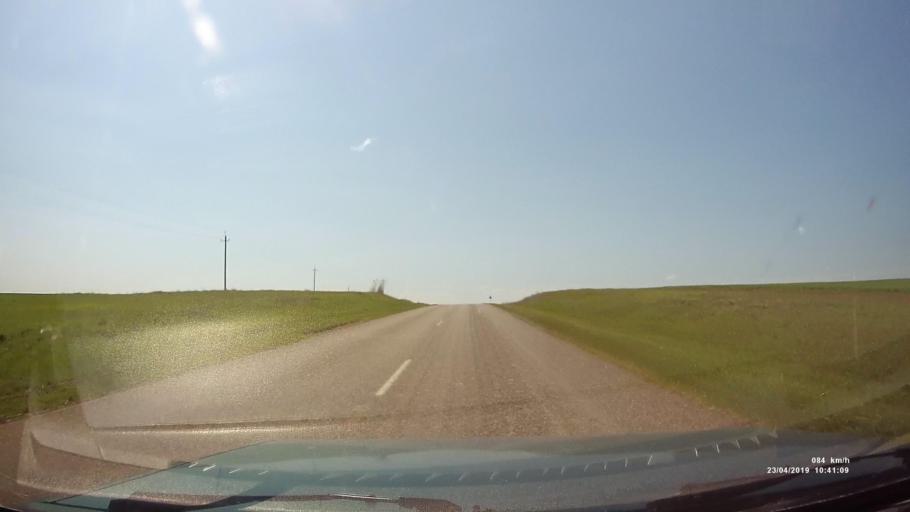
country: RU
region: Kalmykiya
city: Yashalta
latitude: 46.4974
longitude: 42.6383
